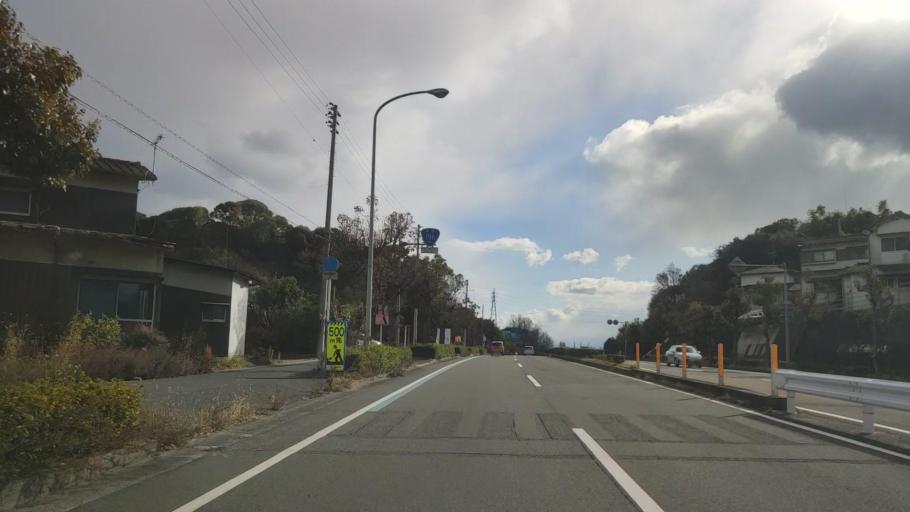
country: JP
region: Ehime
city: Hojo
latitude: 34.0578
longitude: 132.9723
